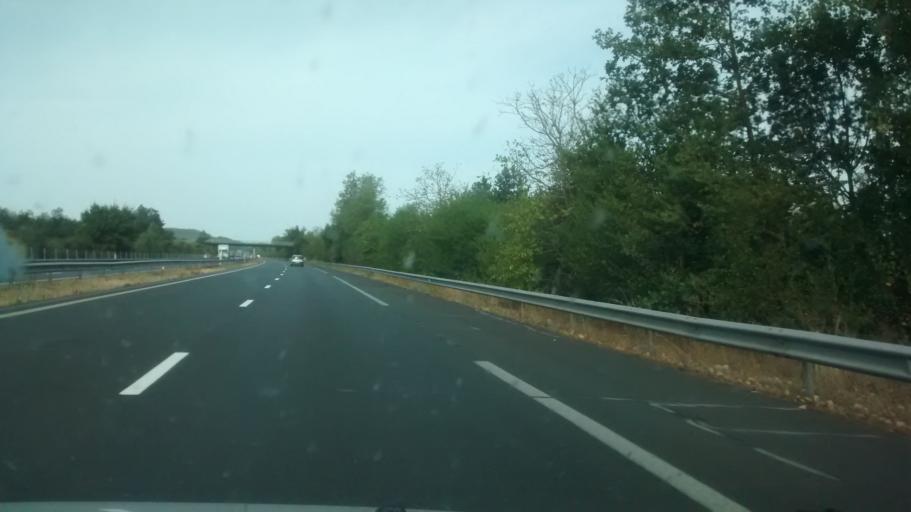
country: FR
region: Aquitaine
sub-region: Departement du Lot-et-Garonne
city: Roquefort
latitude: 44.1844
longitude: 0.5535
